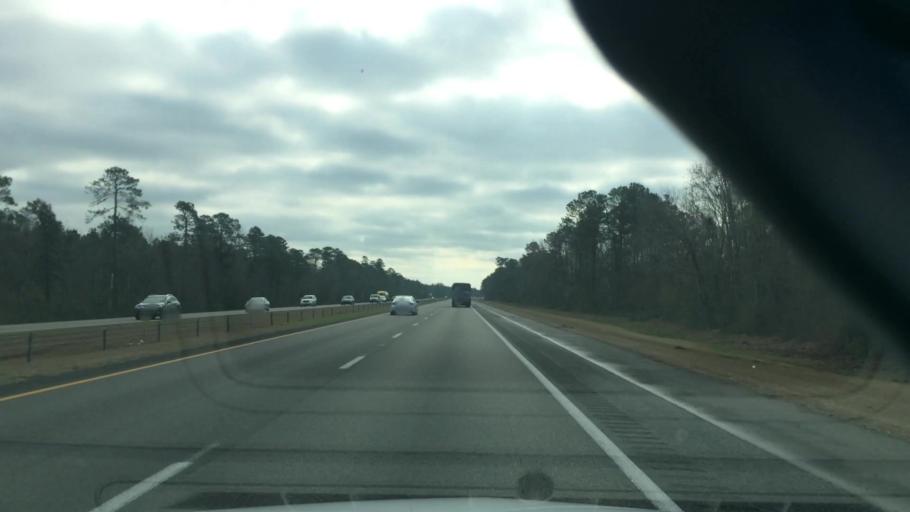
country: US
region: North Carolina
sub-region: Pender County
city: Rocky Point
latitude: 34.4014
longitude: -77.8728
